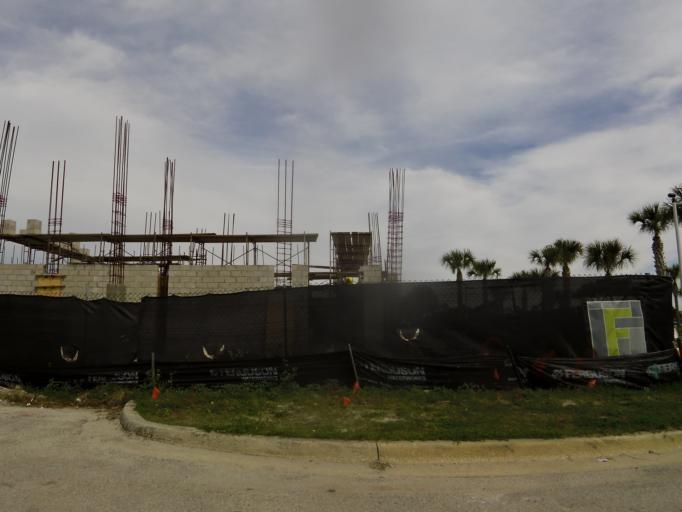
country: US
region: Florida
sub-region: Saint Johns County
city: Villano Beach
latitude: 29.9169
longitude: -81.2946
